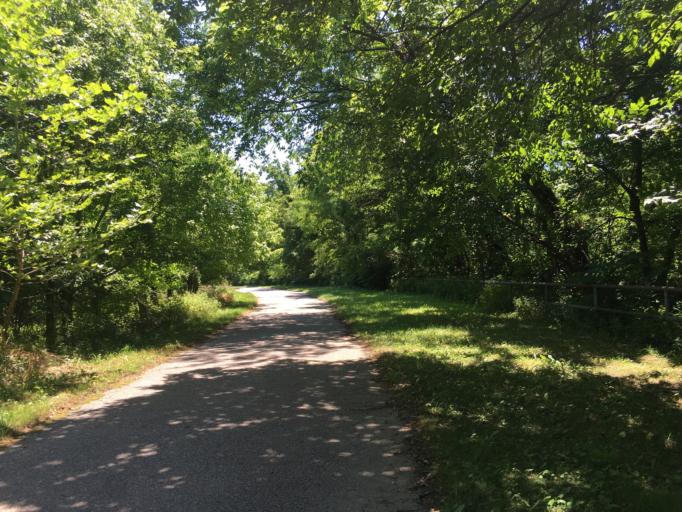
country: US
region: Maryland
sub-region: Baltimore County
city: Lansdowne
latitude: 39.2732
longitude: -76.6530
